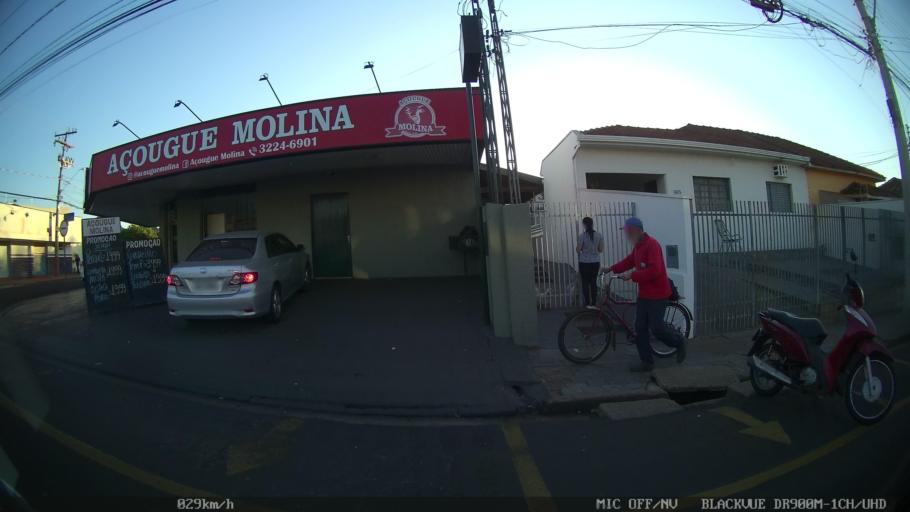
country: BR
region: Sao Paulo
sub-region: Sao Jose Do Rio Preto
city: Sao Jose do Rio Preto
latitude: -20.7893
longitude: -49.3694
